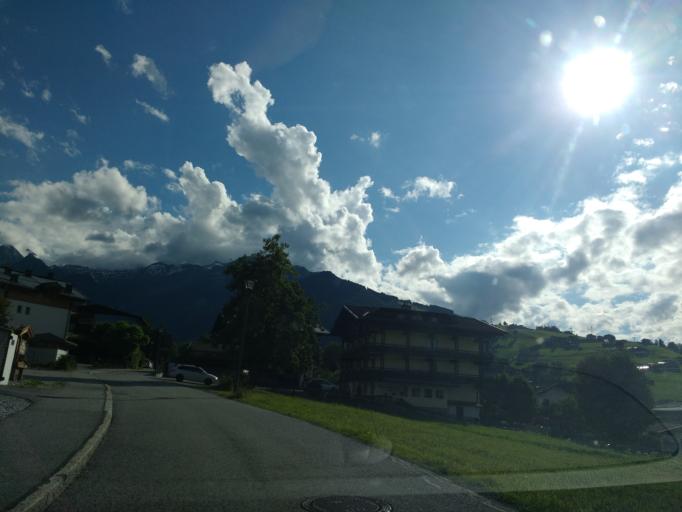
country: AT
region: Salzburg
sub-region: Politischer Bezirk Zell am See
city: Kaprun
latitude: 47.2720
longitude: 12.7632
